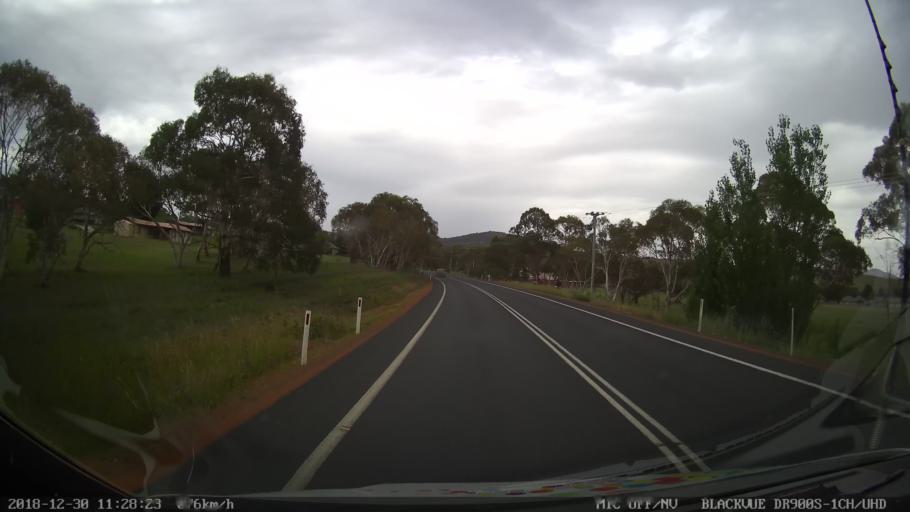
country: AU
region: New South Wales
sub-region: Snowy River
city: Jindabyne
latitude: -36.4530
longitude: 148.6184
